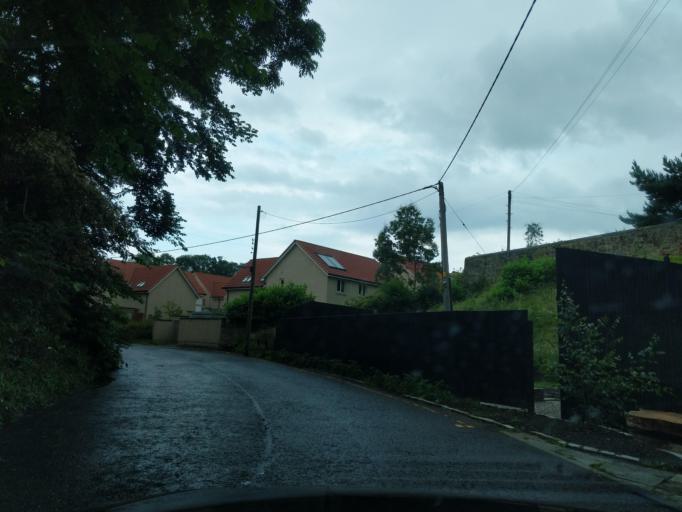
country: GB
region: Scotland
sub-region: Midlothian
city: Dalkeith
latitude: 55.8939
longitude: -3.0775
